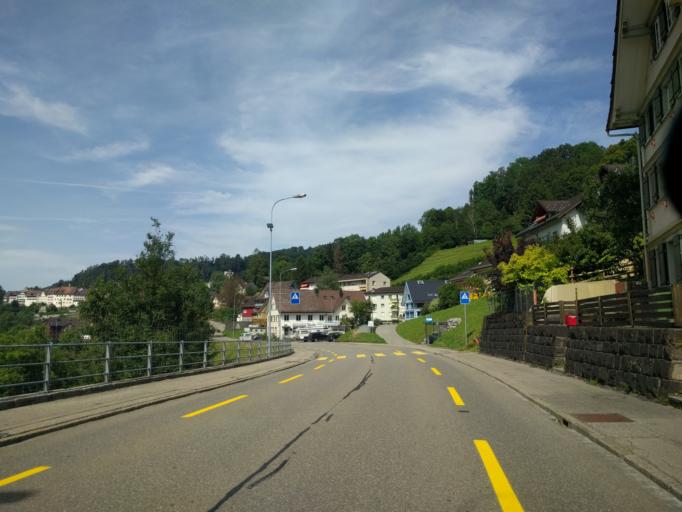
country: CH
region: Saint Gallen
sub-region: Wahlkreis Toggenburg
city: Lichtensteig
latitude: 47.3171
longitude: 9.0861
